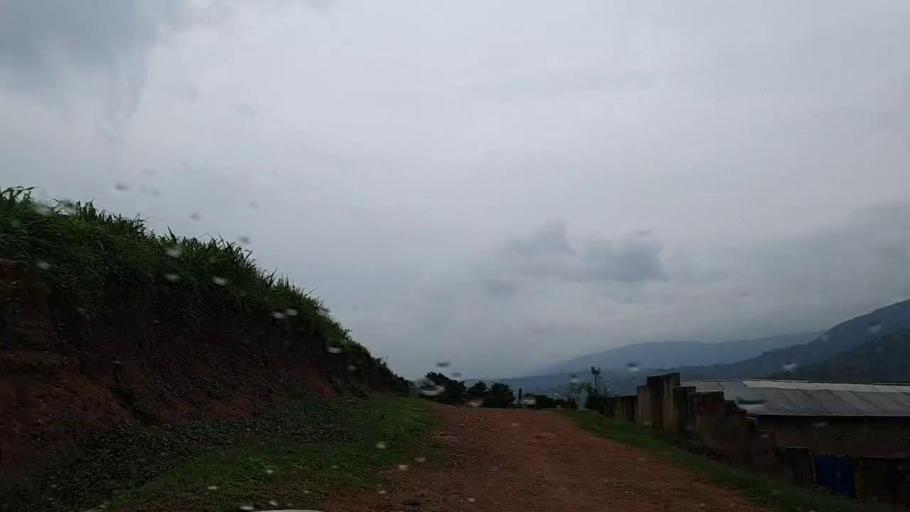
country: RW
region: Kigali
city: Kigali
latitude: -1.9016
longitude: 29.9551
